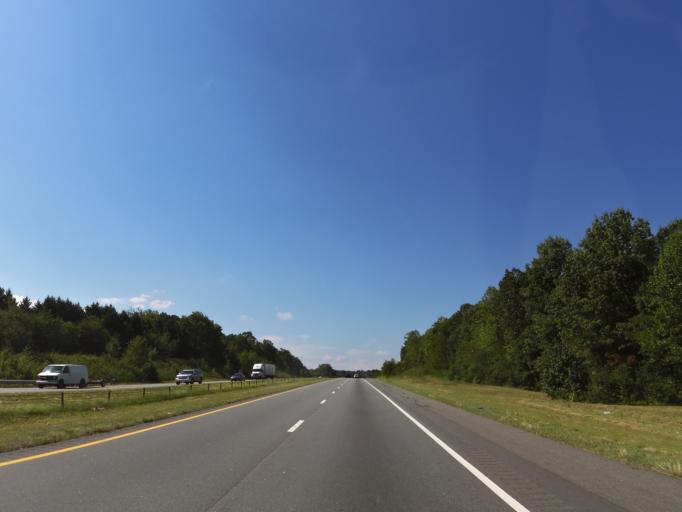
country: US
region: North Carolina
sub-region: Catawba County
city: Mountain View
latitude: 35.6711
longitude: -81.3333
